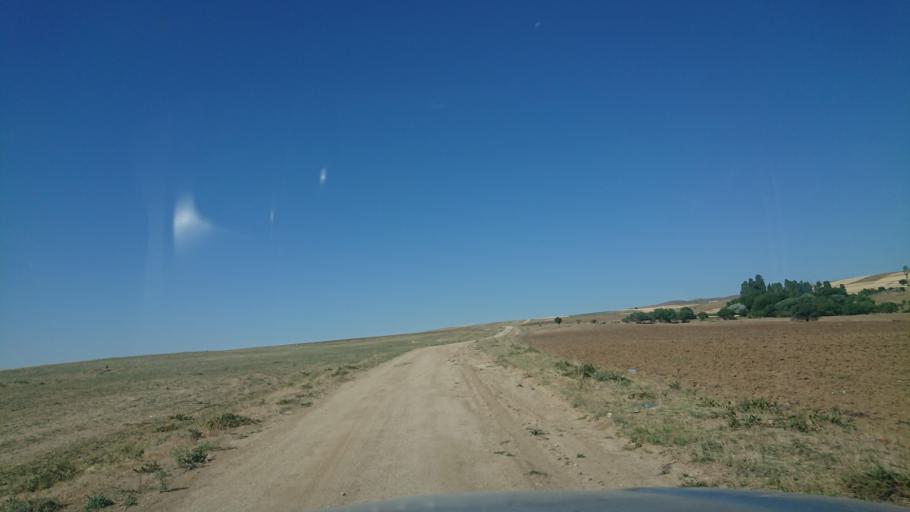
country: TR
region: Aksaray
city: Sariyahsi
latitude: 38.9341
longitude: 33.8627
